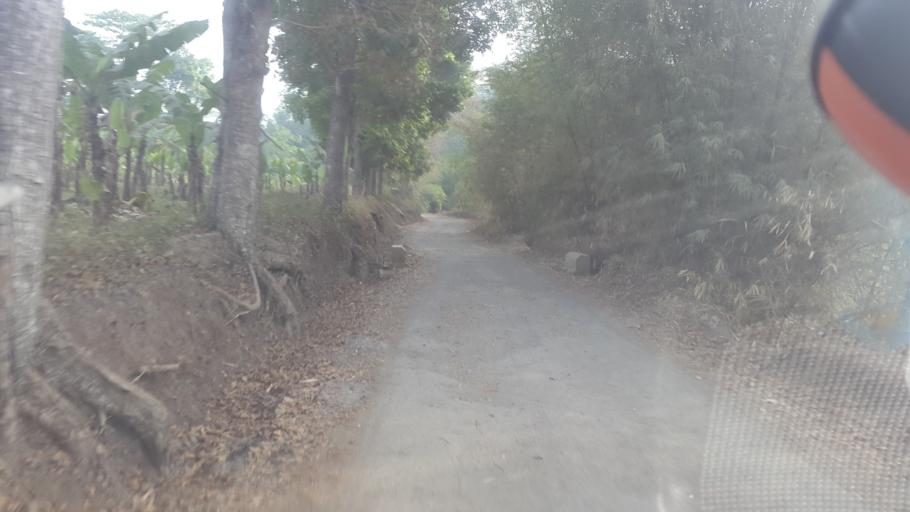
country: ID
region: West Java
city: Cilandak
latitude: -6.9463
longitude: 106.7489
